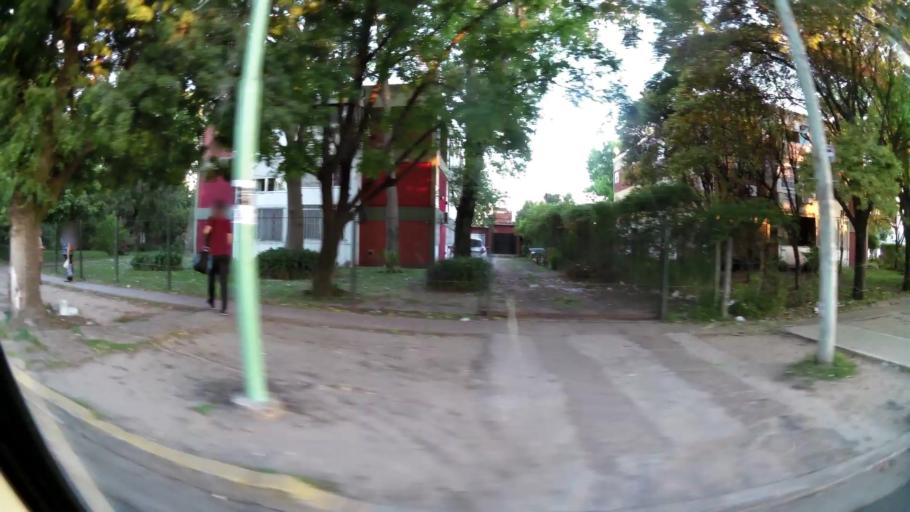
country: AR
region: Buenos Aires
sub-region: Partido de Quilmes
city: Quilmes
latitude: -34.8076
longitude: -58.1854
